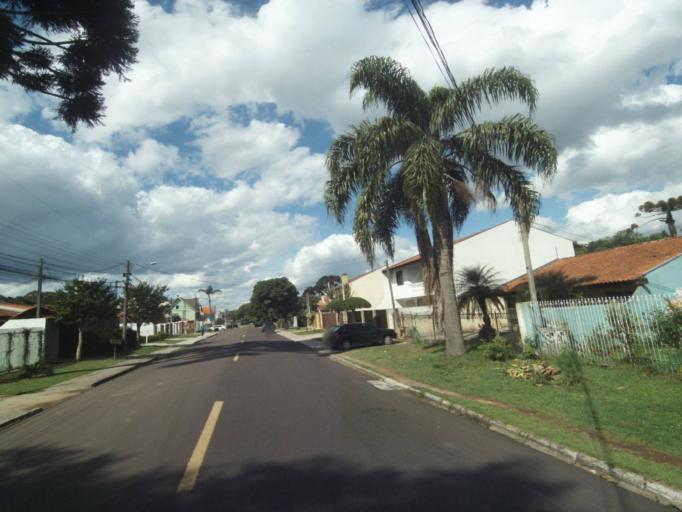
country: BR
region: Parana
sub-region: Curitiba
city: Curitiba
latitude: -25.4365
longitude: -49.3468
